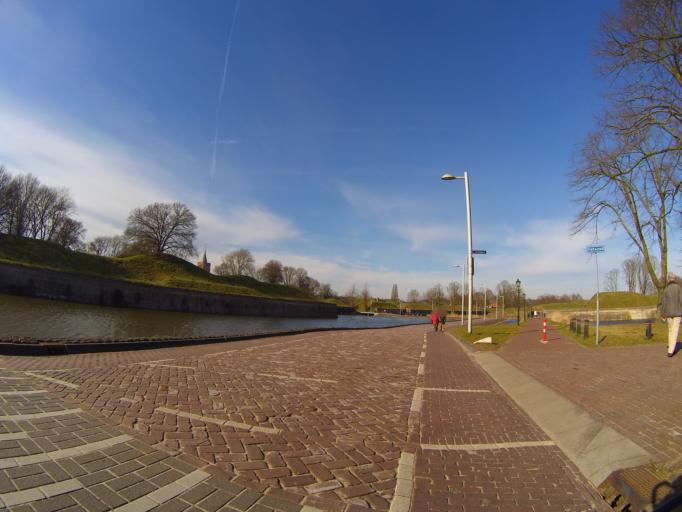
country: NL
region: North Holland
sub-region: Gemeente Naarden
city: Naarden
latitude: 52.2935
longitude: 5.1670
